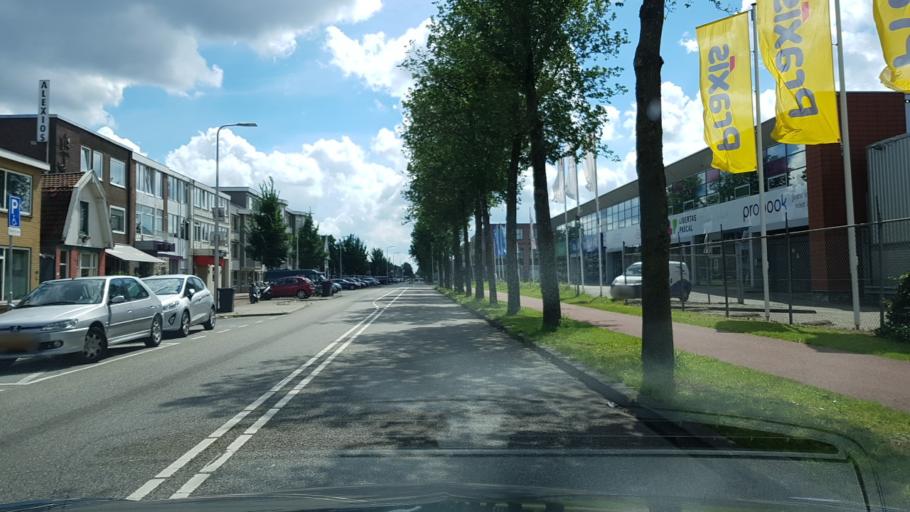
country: NL
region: Utrecht
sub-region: Stichtse Vecht
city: Maarssen
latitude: 52.1134
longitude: 5.0781
